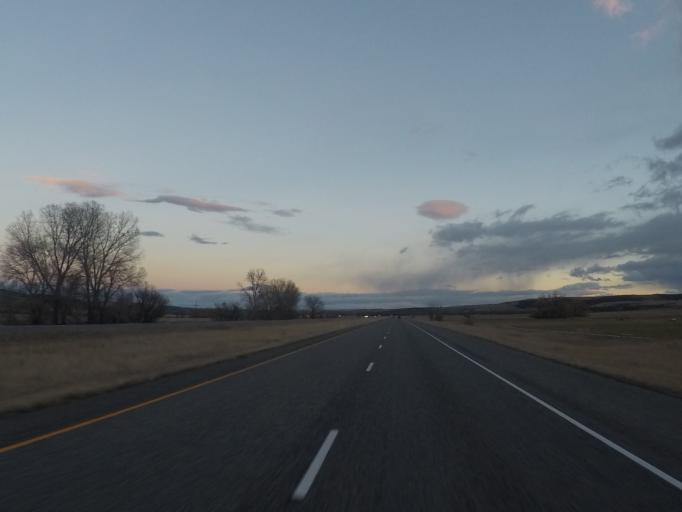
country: US
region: Montana
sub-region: Sweet Grass County
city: Big Timber
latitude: 45.8088
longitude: -109.8600
